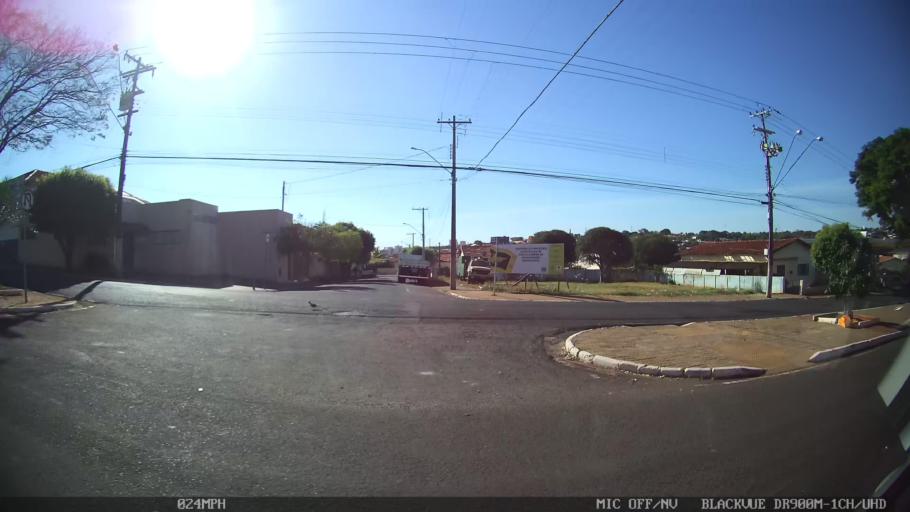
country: BR
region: Sao Paulo
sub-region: Olimpia
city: Olimpia
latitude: -20.7445
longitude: -48.9076
